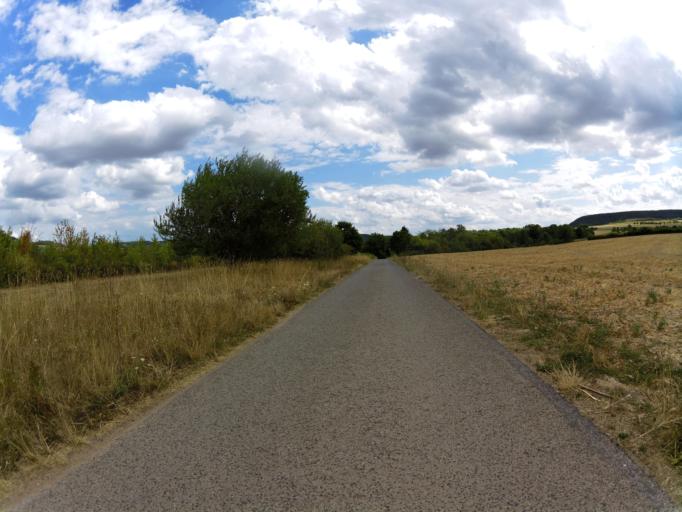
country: DE
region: Bavaria
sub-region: Regierungsbezirk Unterfranken
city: Zellingen
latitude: 49.8859
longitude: 9.8270
